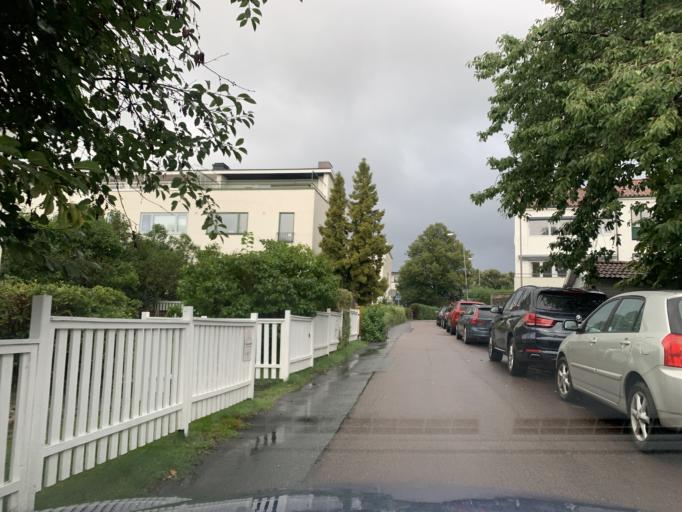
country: SE
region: Vaestra Goetaland
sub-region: Goteborg
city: Goeteborg
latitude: 57.7026
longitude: 12.0097
